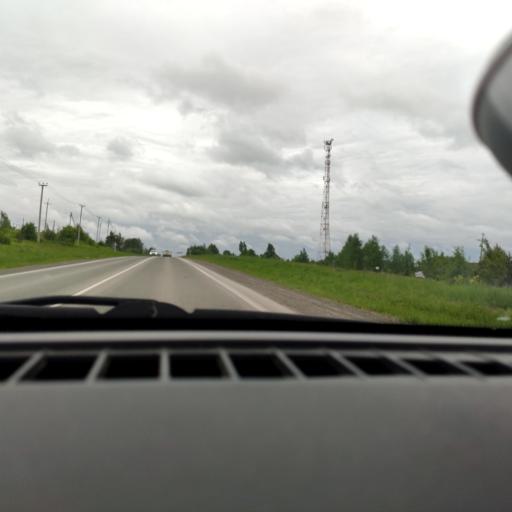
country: RU
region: Perm
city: Ust'-Kachka
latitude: 57.9459
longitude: 55.7388
